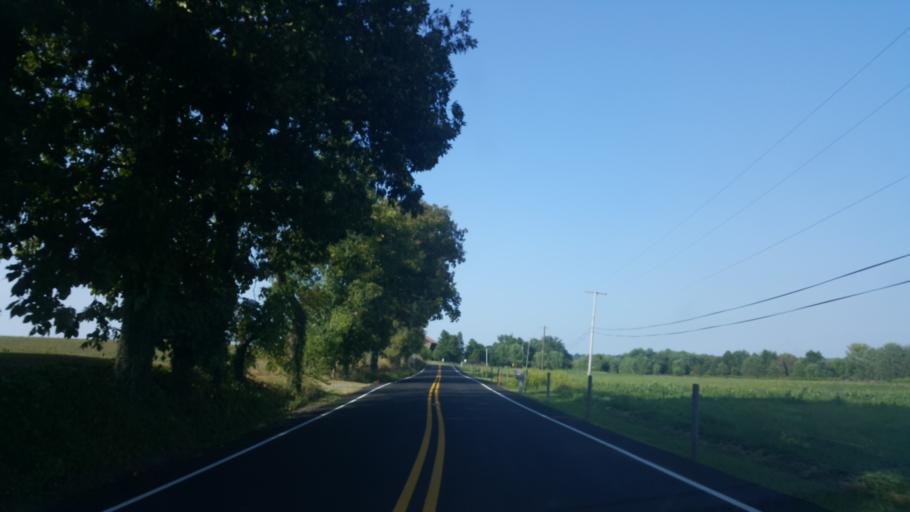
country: US
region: Pennsylvania
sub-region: Lebanon County
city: Campbelltown
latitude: 40.2211
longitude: -76.5571
